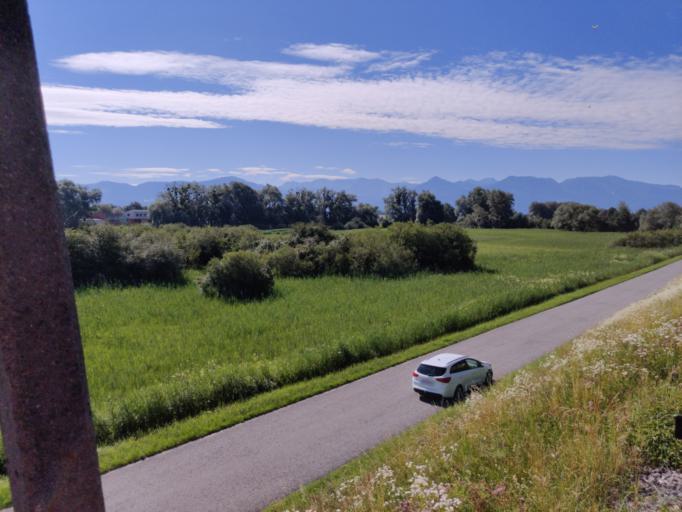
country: AT
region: Vorarlberg
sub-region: Politischer Bezirk Bregenz
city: Fussach
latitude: 47.4820
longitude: 9.6715
